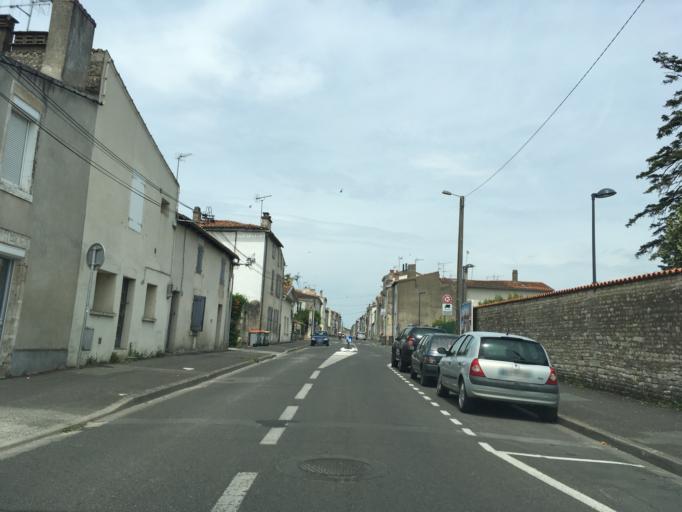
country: FR
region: Poitou-Charentes
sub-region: Departement des Deux-Sevres
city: Niort
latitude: 46.3153
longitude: -0.4634
